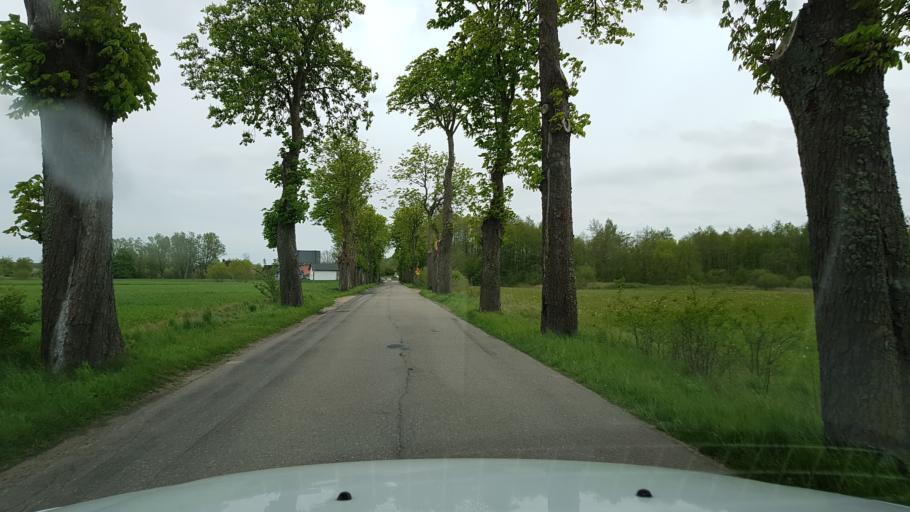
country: PL
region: West Pomeranian Voivodeship
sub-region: Powiat slawienski
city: Slawno
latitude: 54.4634
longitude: 16.7340
